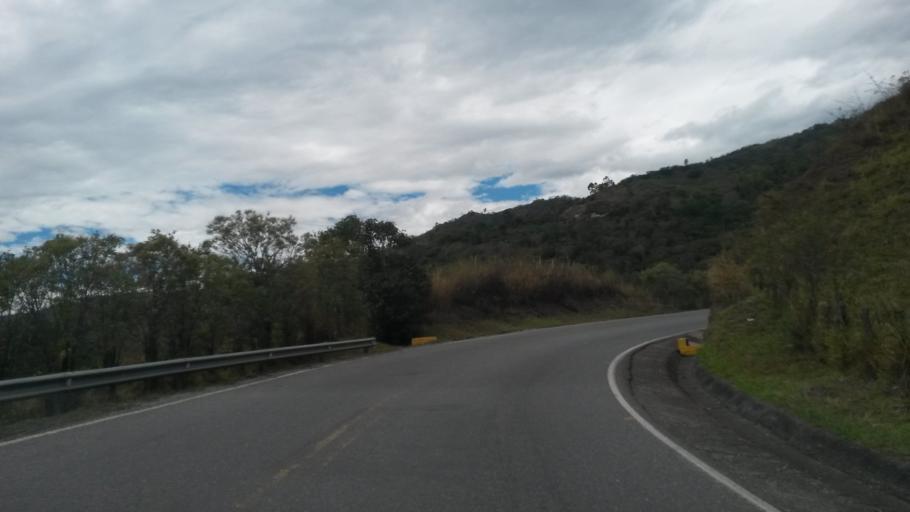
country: CO
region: Cauca
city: Rosas
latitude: 2.2796
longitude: -76.7082
